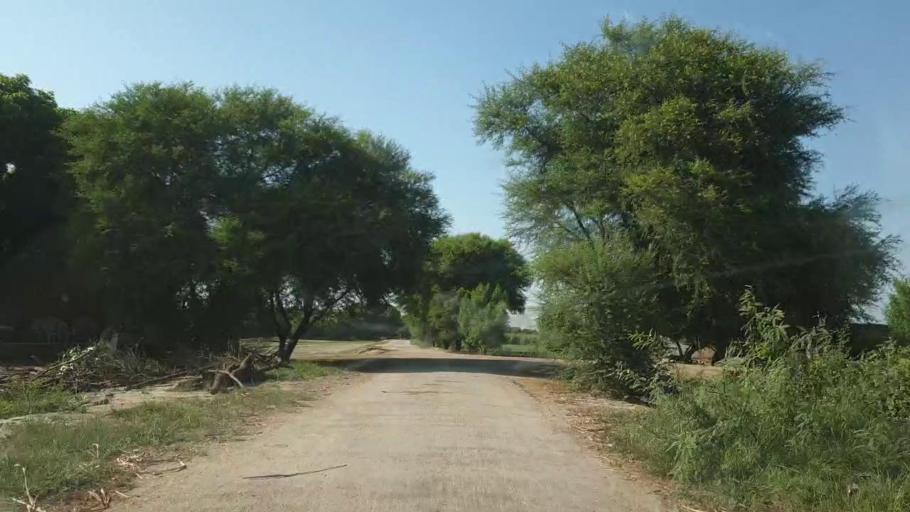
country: PK
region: Sindh
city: Tando Jam
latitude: 25.3436
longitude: 68.5844
